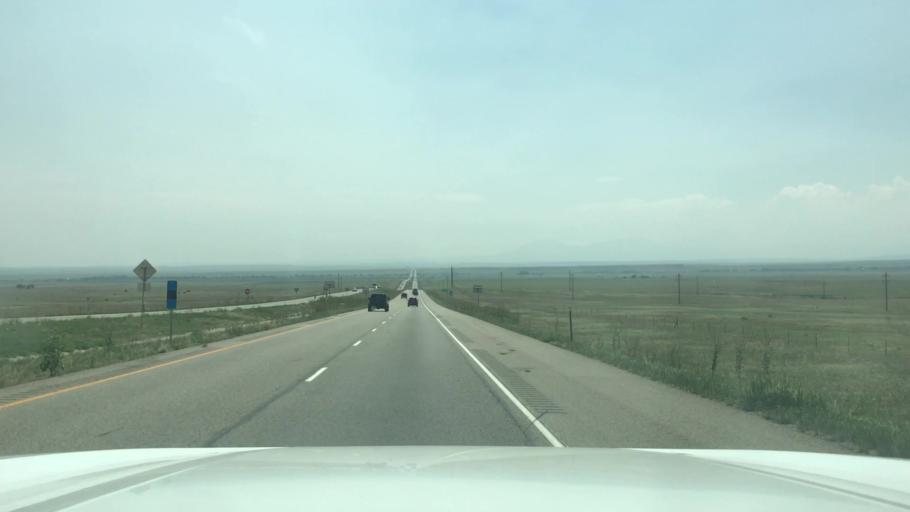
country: US
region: Colorado
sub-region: Pueblo County
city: Colorado City
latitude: 37.8935
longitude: -104.8293
